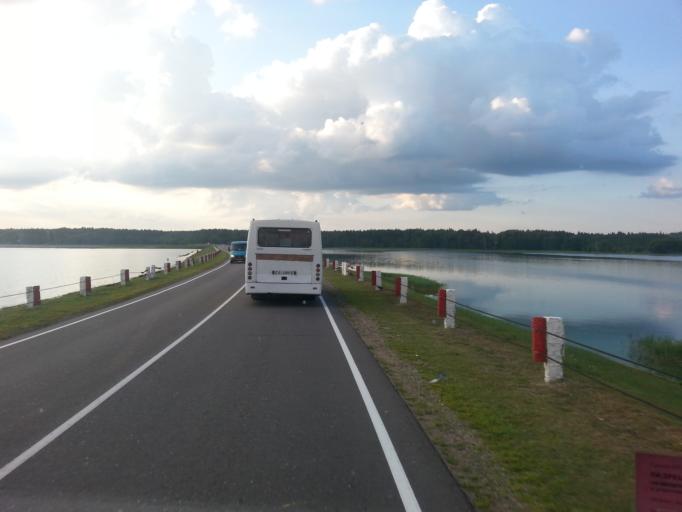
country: BY
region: Minsk
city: Il'ya
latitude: 54.5040
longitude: 27.2304
